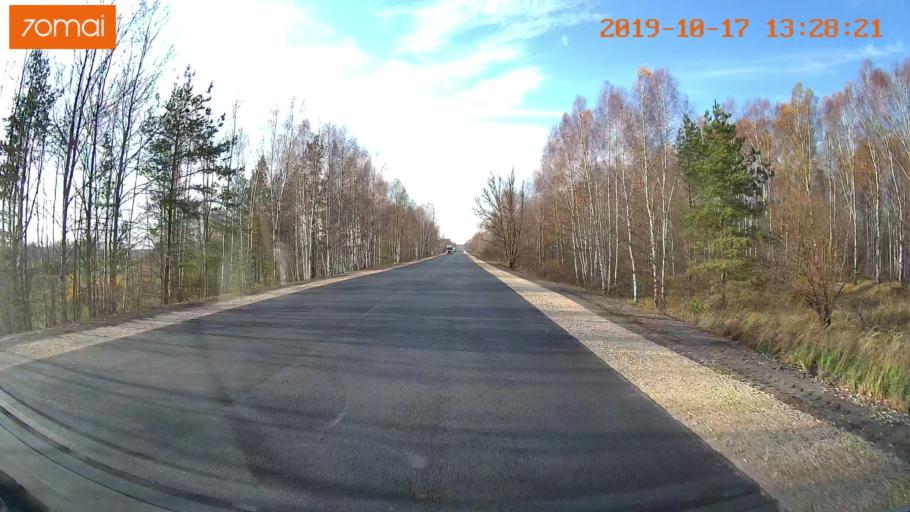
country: RU
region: Vladimir
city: Velikodvorskiy
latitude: 55.1159
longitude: 40.8712
